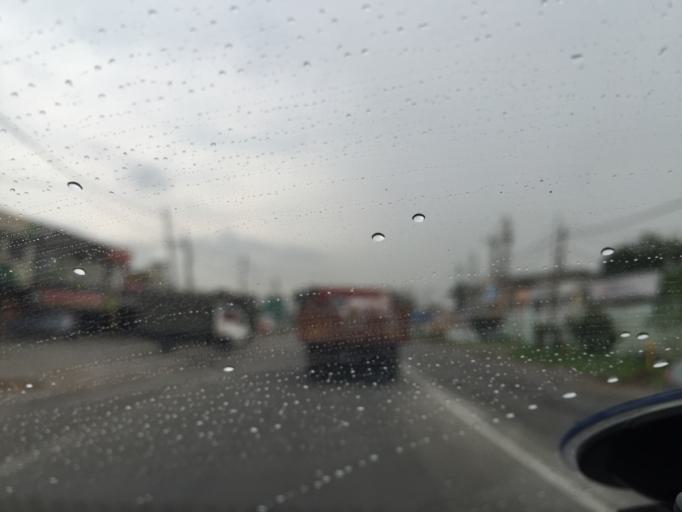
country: MY
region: Selangor
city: Subang Jaya
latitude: 3.0134
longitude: 101.5233
